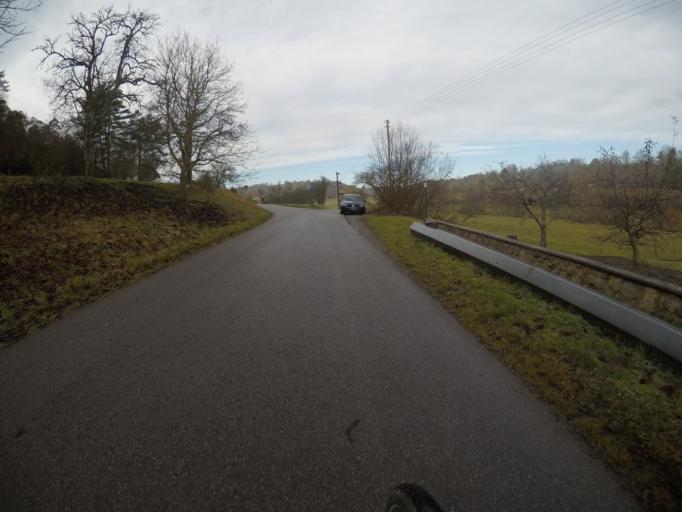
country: DE
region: Baden-Wuerttemberg
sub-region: Karlsruhe Region
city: Gechingen
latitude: 48.6780
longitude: 8.8463
